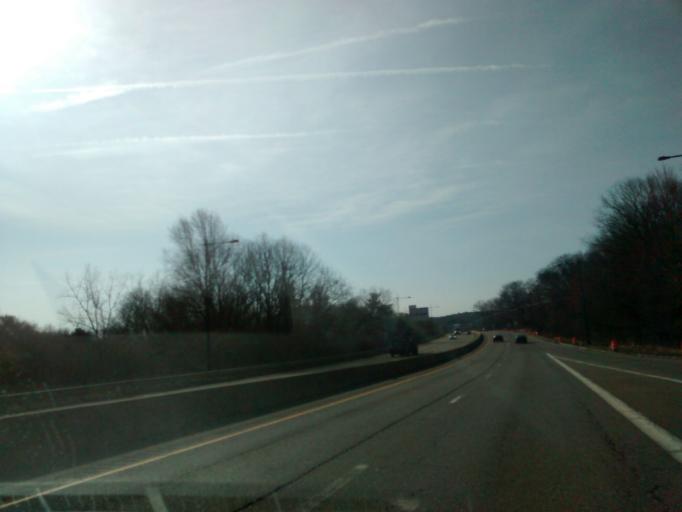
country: US
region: Massachusetts
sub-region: Worcester County
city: Millbury
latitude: 42.1982
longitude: -71.7743
